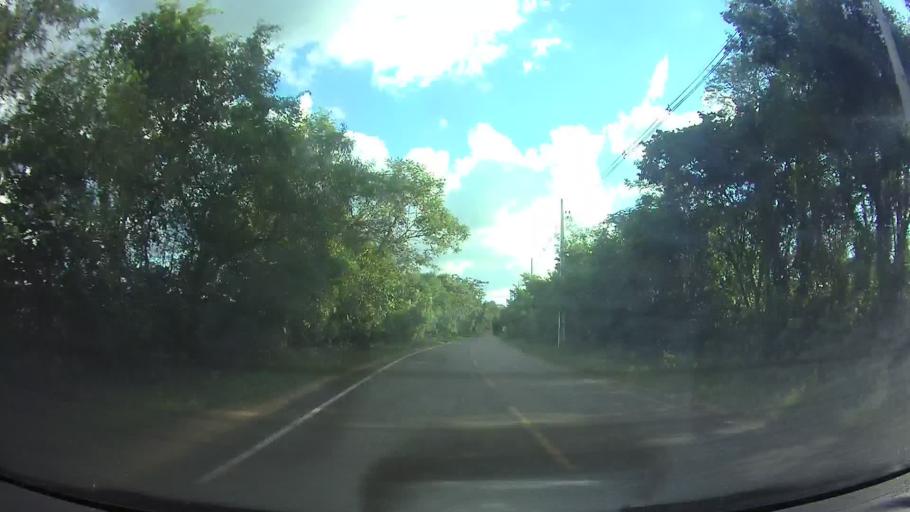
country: PY
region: Cordillera
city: Altos
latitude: -25.2245
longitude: -57.2255
